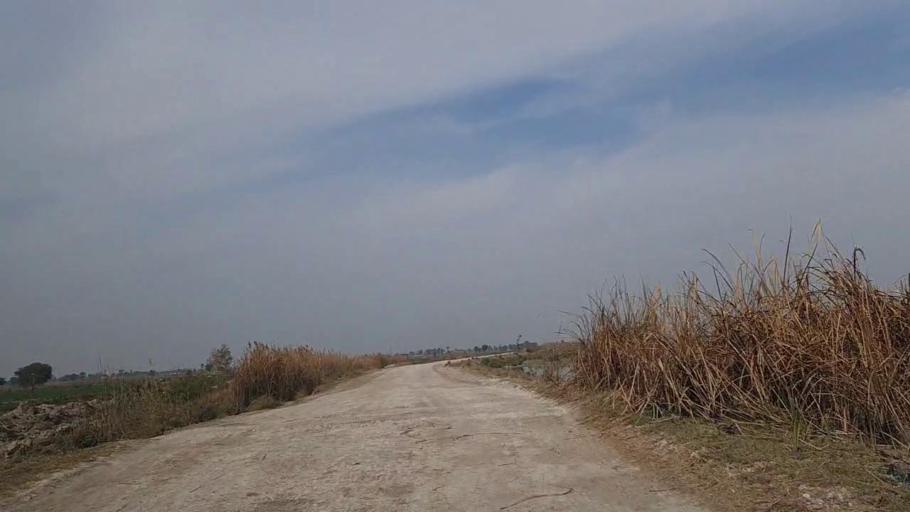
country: PK
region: Sindh
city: Daur
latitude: 26.4696
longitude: 68.4025
